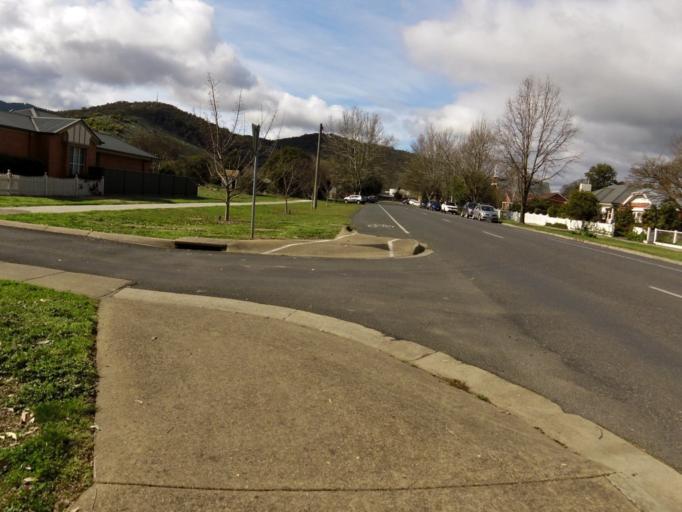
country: AU
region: Victoria
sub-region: Wangaratta
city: Wangaratta
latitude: -36.5587
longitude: 146.7227
